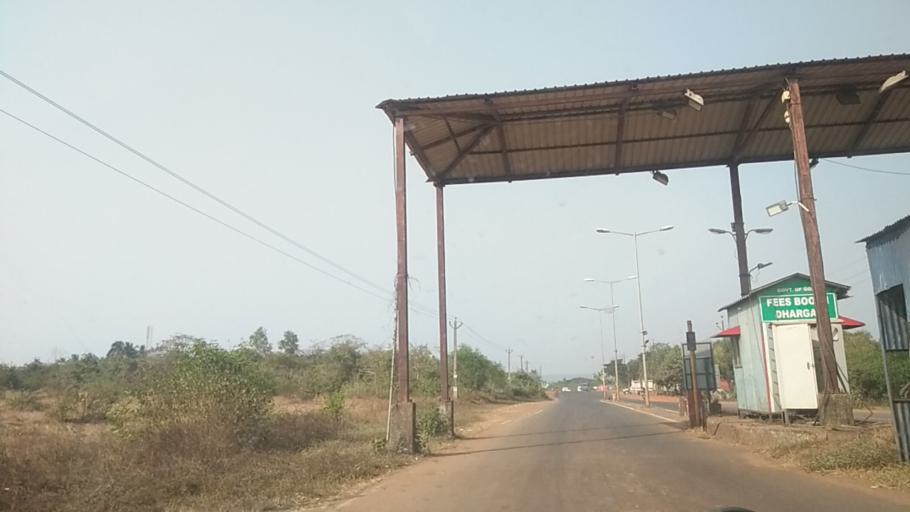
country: IN
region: Goa
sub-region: North Goa
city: Colovale
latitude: 15.6631
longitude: 73.8386
